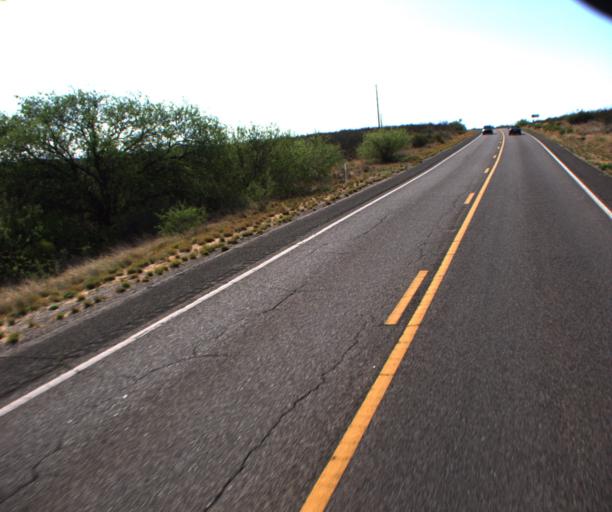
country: US
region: Arizona
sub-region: Cochise County
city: Tombstone
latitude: 31.7875
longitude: -110.1476
